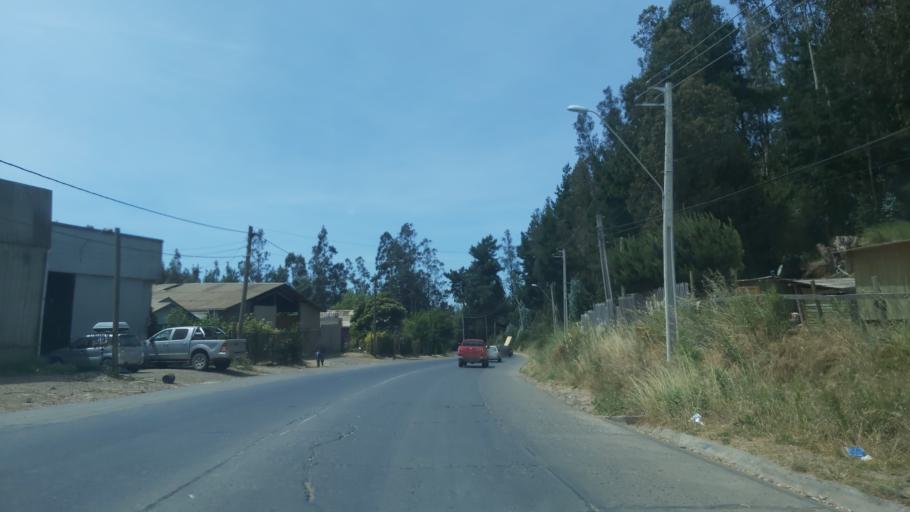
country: CL
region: Maule
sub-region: Provincia de Talca
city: Constitucion
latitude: -35.3521
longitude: -72.4098
